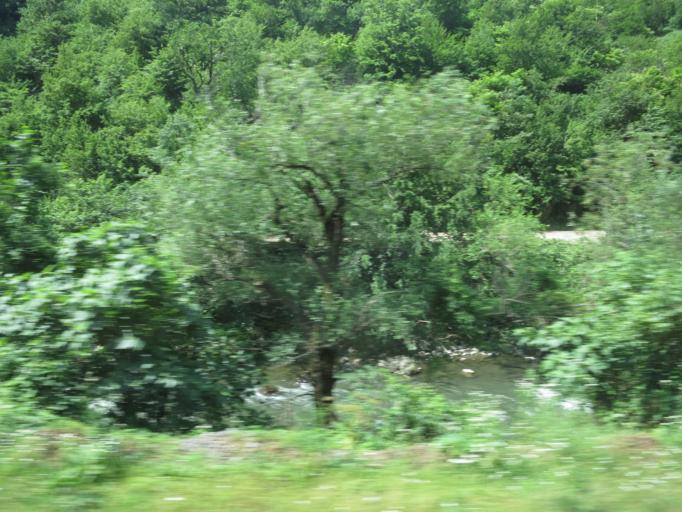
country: GE
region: Imereti
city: Kharagauli
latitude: 42.0068
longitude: 43.2154
